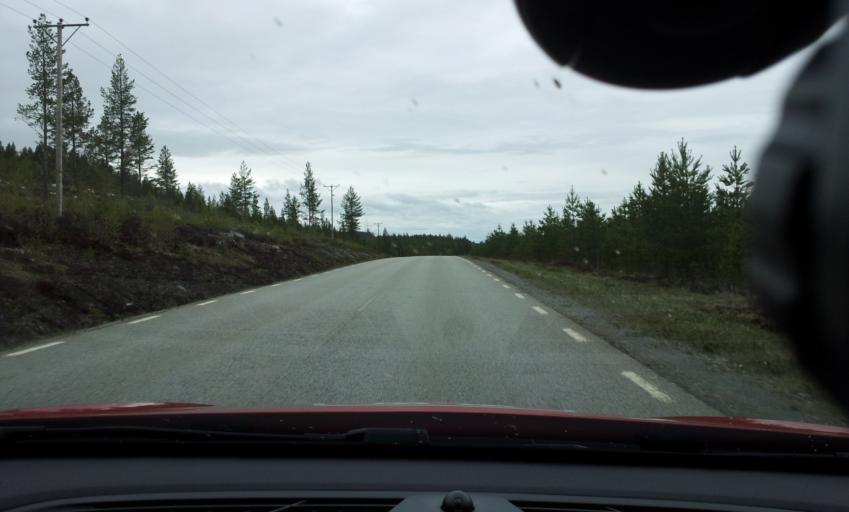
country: SE
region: Jaemtland
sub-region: Bergs Kommun
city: Hoverberg
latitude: 62.7095
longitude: 14.6123
